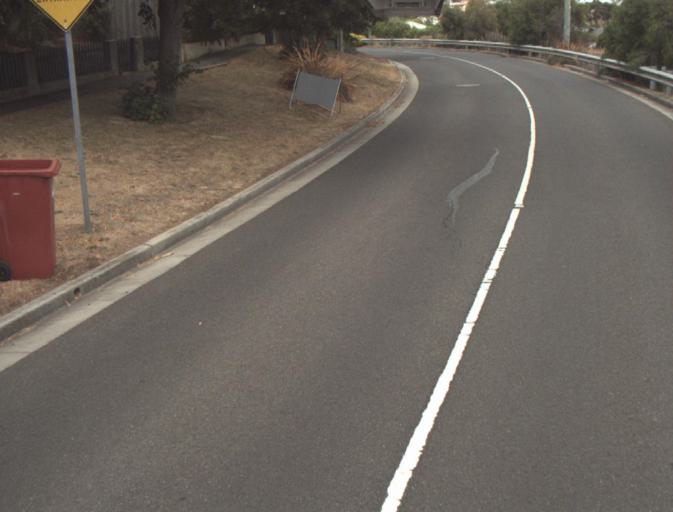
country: AU
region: Tasmania
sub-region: Launceston
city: East Launceston
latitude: -41.4533
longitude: 147.1485
